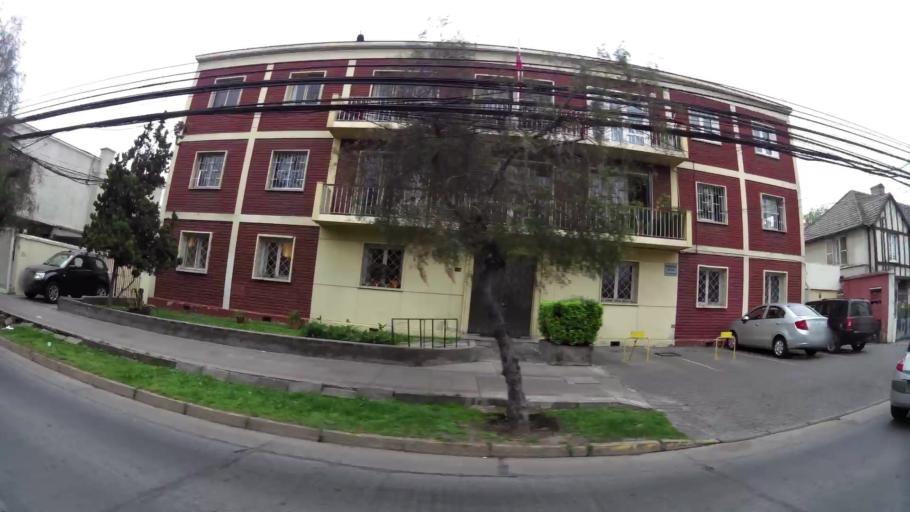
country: CL
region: Santiago Metropolitan
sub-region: Provincia de Santiago
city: Santiago
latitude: -33.4385
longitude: -70.6176
